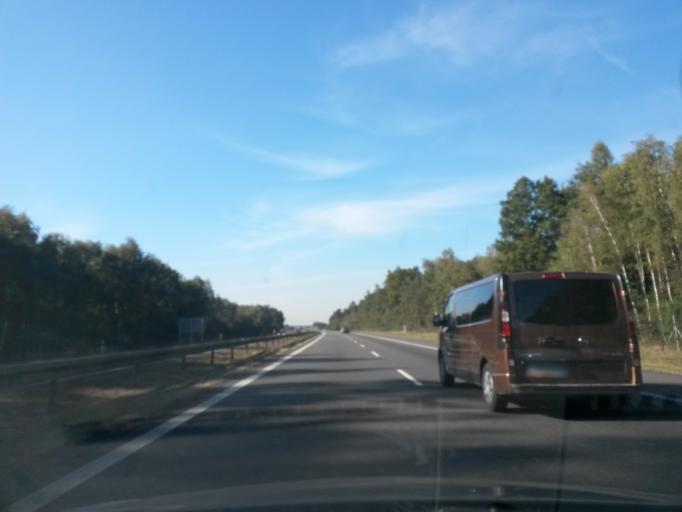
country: PL
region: Opole Voivodeship
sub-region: Powiat opolski
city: Proszkow
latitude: 50.5544
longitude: 17.8858
